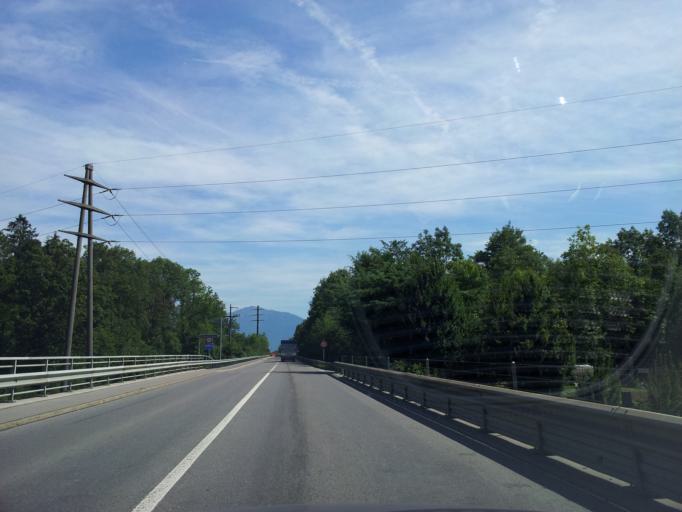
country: CH
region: Schwyz
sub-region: Bezirk March
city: Lachen
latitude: 47.1927
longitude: 8.8670
